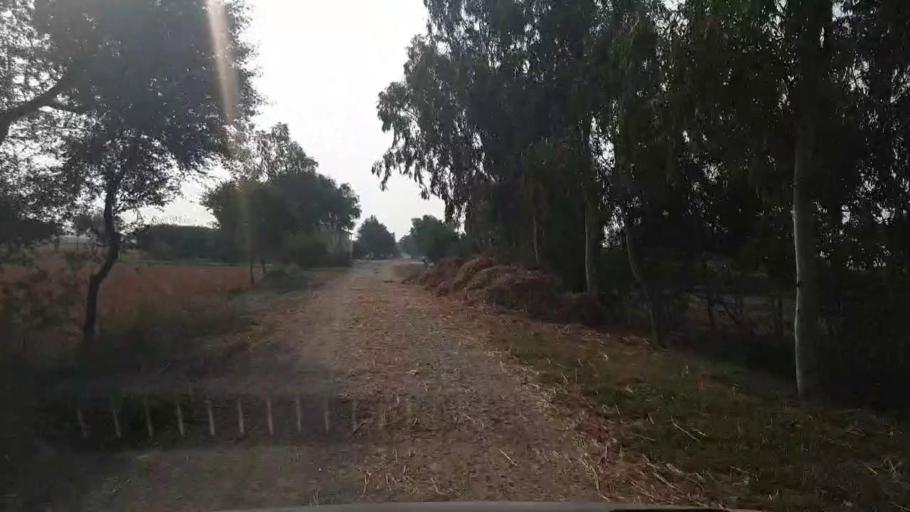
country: PK
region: Sindh
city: Tando Muhammad Khan
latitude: 25.0957
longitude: 68.5039
